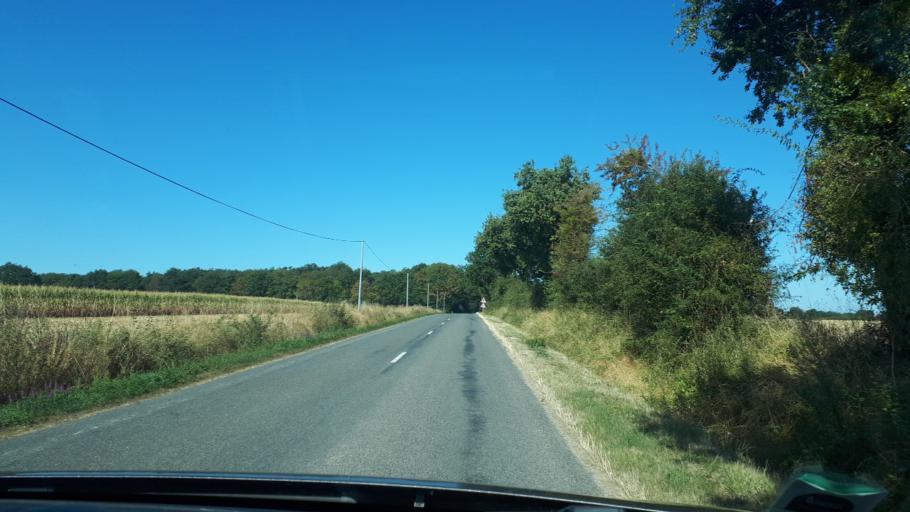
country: FR
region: Centre
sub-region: Departement du Loiret
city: Briare
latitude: 47.5928
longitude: 2.7117
